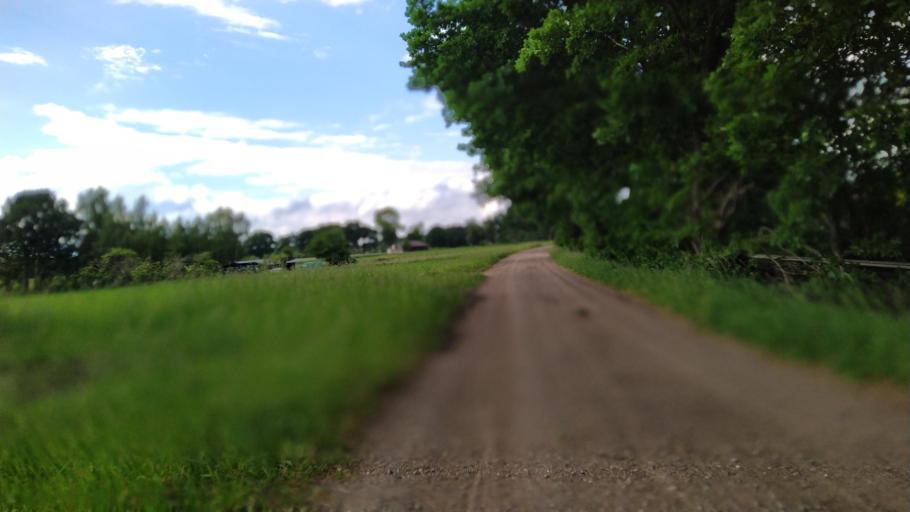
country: DE
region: Lower Saxony
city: Sandbostel
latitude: 53.4357
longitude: 9.1710
